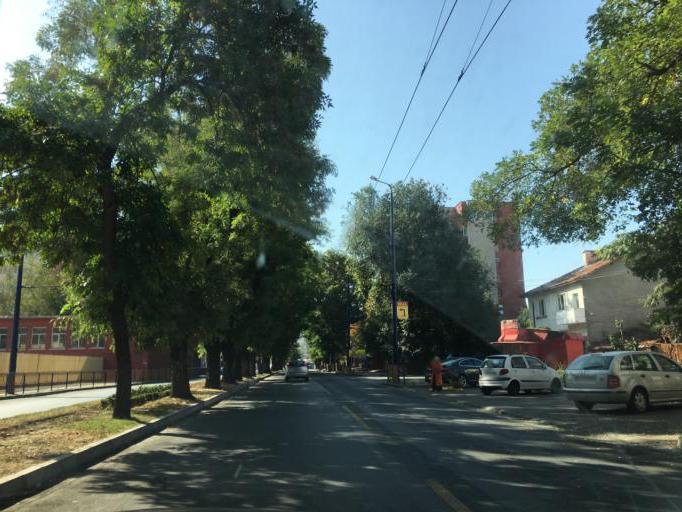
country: BG
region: Pazardzhik
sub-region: Obshtina Pazardzhik
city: Pazardzhik
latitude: 42.1983
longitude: 24.3333
